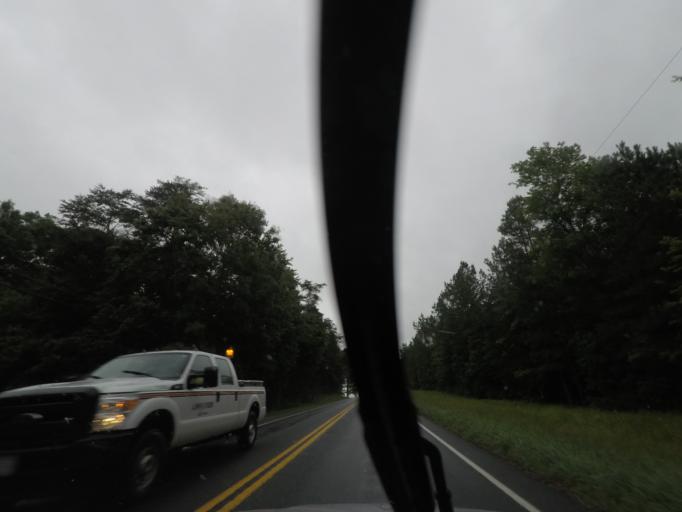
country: US
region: Virginia
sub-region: Orange County
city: Orange
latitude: 38.2965
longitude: -78.1367
